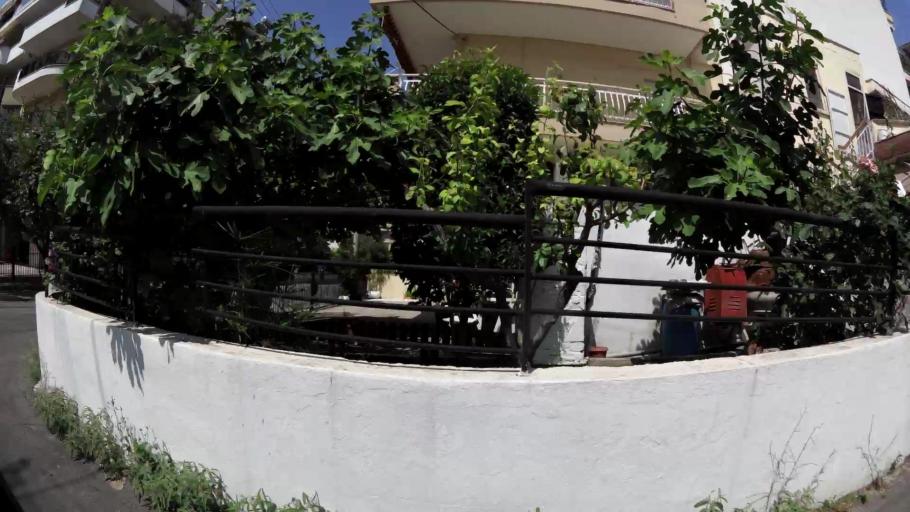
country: GR
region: Central Macedonia
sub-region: Nomos Thessalonikis
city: Evosmos
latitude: 40.6741
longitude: 22.9132
